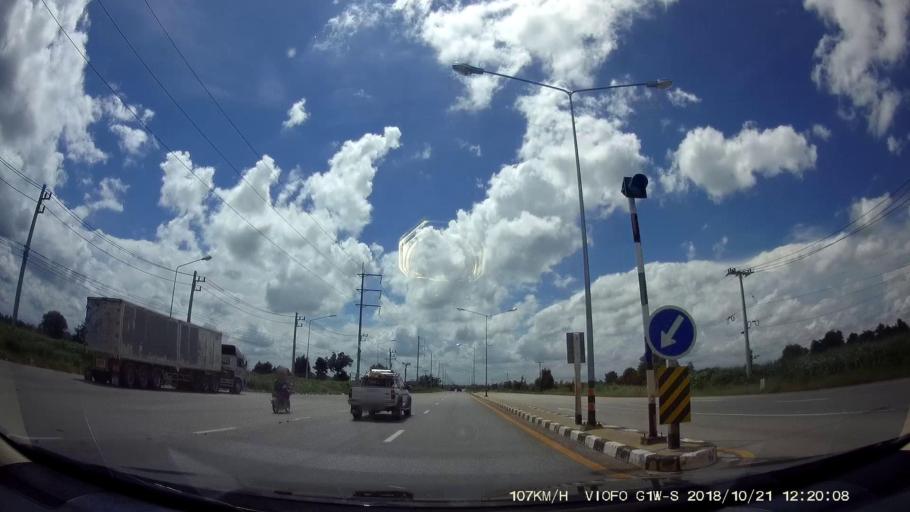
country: TH
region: Nakhon Ratchasima
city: Dan Khun Thot
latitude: 15.2919
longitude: 101.8063
